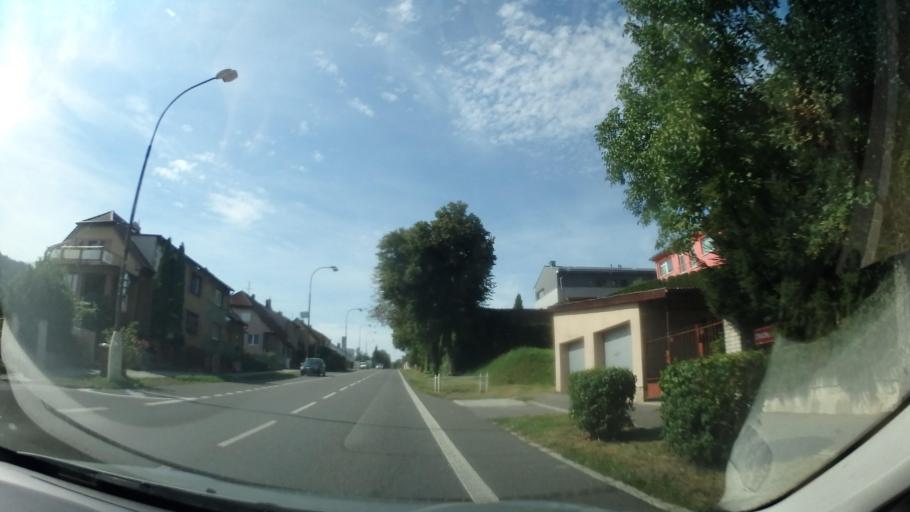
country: CZ
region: Jihocesky
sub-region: Okres Pisek
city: Pisek
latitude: 49.3093
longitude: 14.1302
